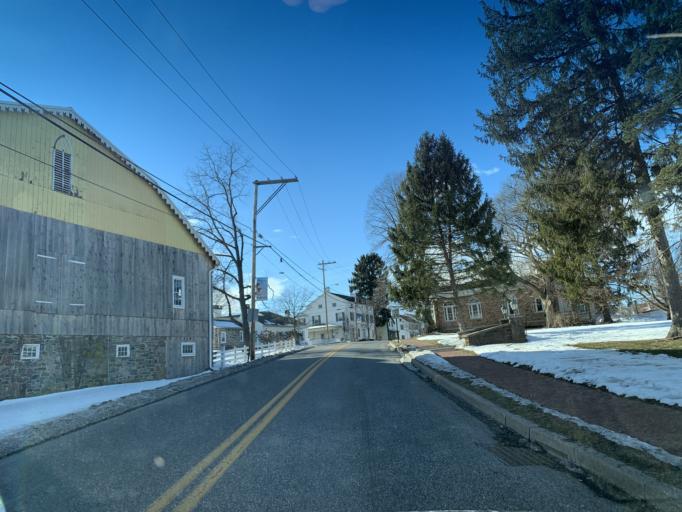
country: US
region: Pennsylvania
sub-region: York County
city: Dover
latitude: 40.0509
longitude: -76.9418
